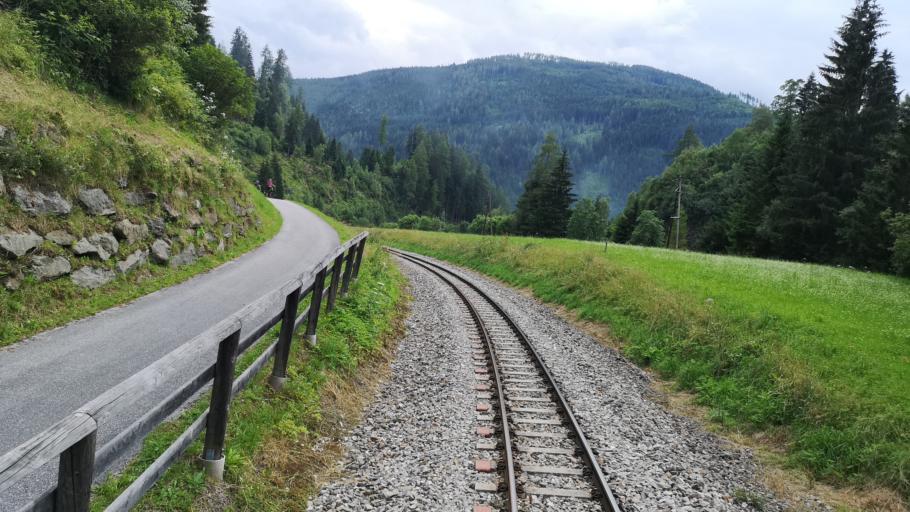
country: AT
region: Salzburg
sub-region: Politischer Bezirk Tamsweg
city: Ramingstein
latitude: 47.0831
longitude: 13.8134
